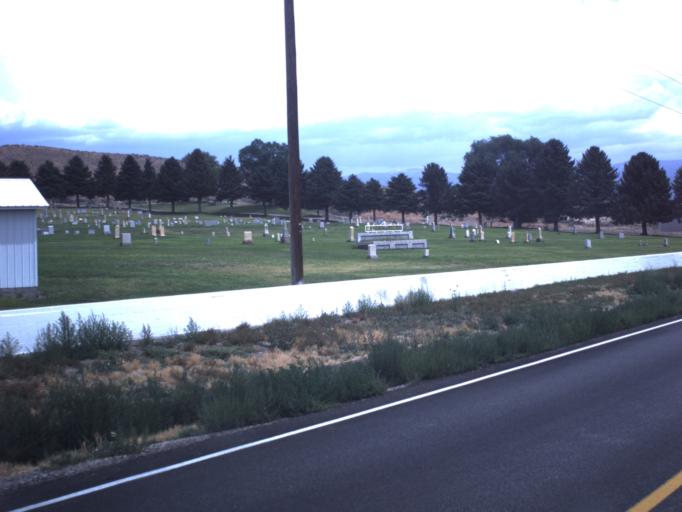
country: US
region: Utah
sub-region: Sanpete County
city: Moroni
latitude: 39.5415
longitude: -111.5956
